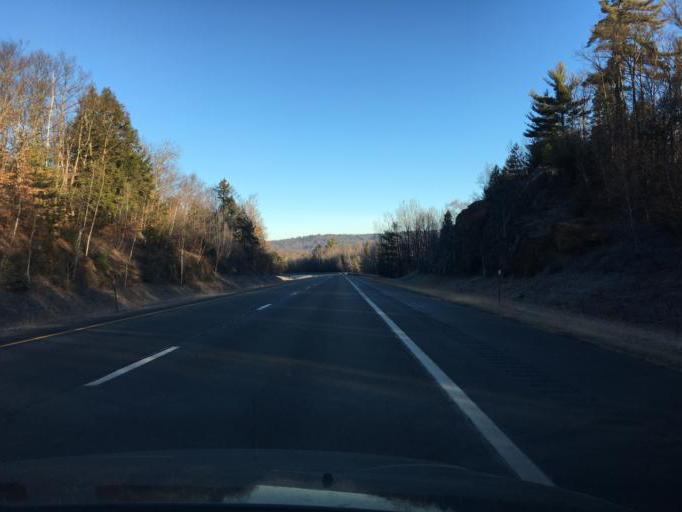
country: US
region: New Hampshire
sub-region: Belknap County
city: Sanbornton
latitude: 43.5581
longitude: -71.6168
